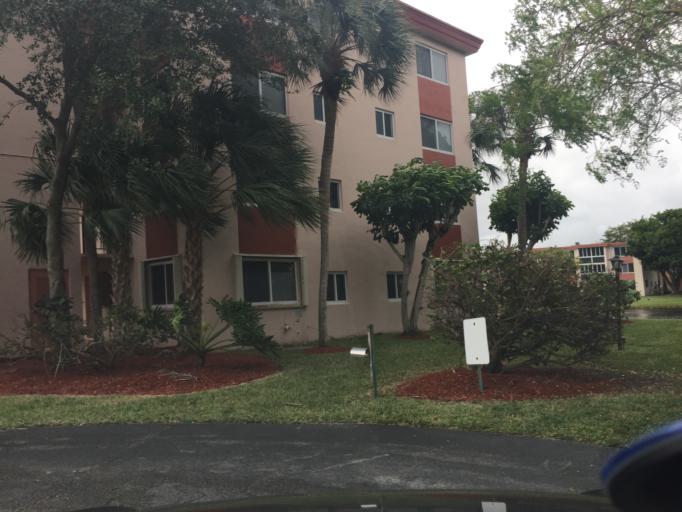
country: US
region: Florida
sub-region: Broward County
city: Plantation
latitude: 26.1385
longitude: -80.2269
